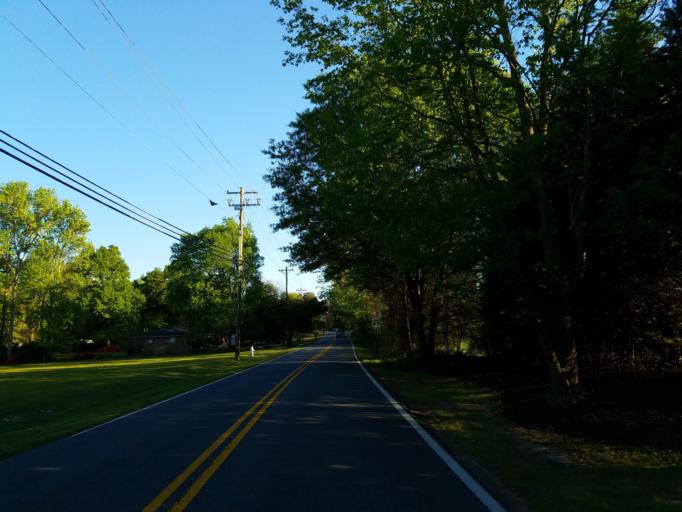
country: US
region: Georgia
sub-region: Cobb County
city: Powder Springs
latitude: 33.9249
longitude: -84.6366
